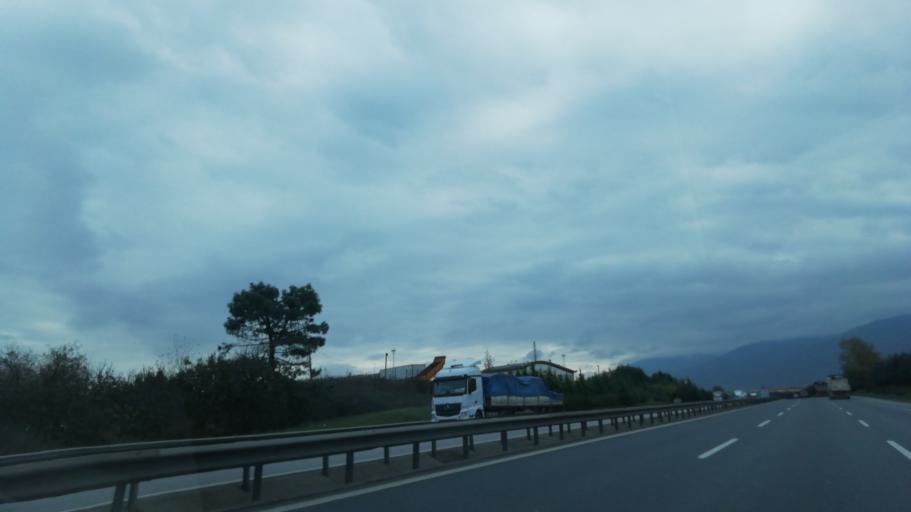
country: TR
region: Kocaeli
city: Kosekoy
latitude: 40.7370
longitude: 30.0490
